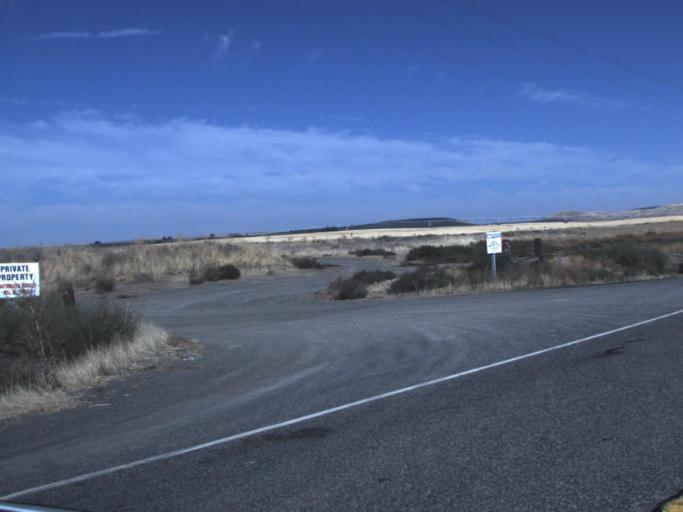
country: US
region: Washington
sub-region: Walla Walla County
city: Burbank
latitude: 46.2897
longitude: -118.7356
